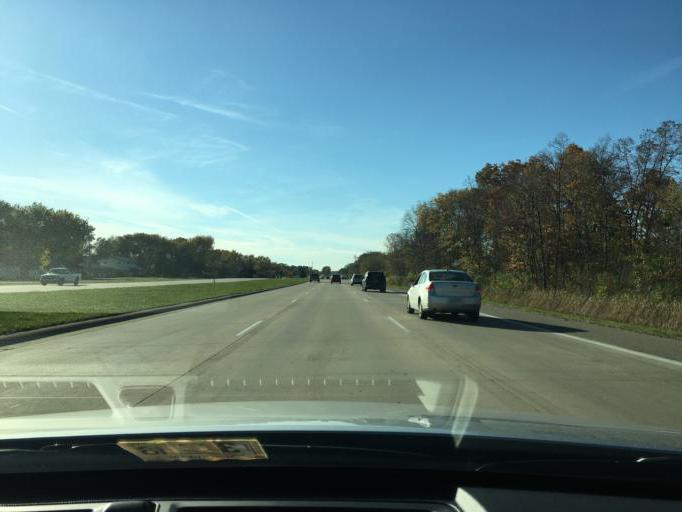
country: US
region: Michigan
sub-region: Macomb County
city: Clinton
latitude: 42.5691
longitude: -82.9210
